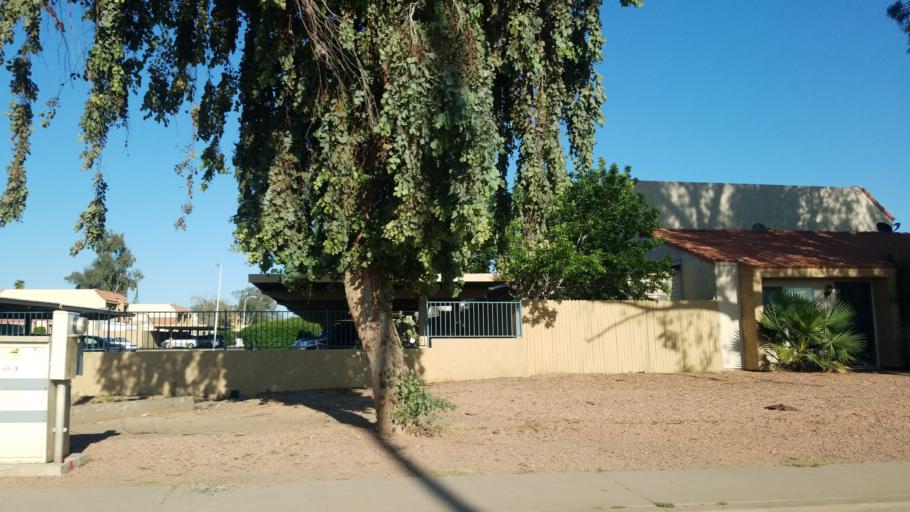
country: US
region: Arizona
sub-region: Maricopa County
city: Glendale
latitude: 33.5279
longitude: -112.1644
